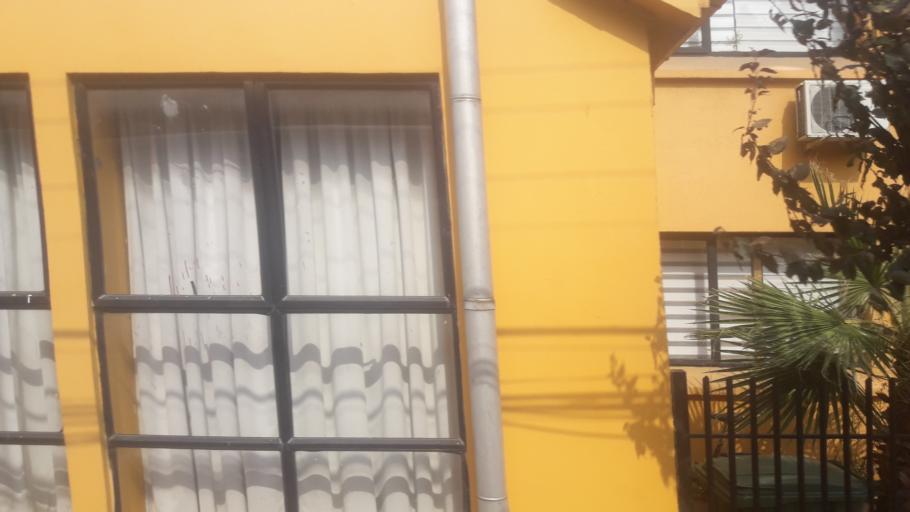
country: CL
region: Biobio
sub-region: Provincia de Concepcion
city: Lota
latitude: -37.1751
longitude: -72.9369
